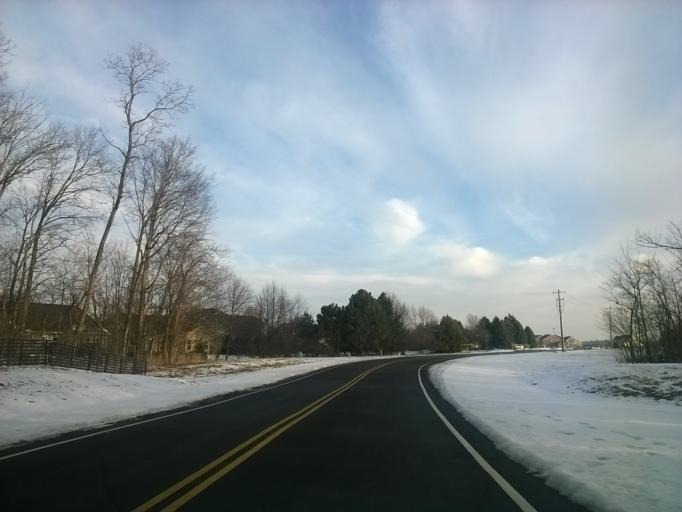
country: US
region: Indiana
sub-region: Hamilton County
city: Fishers
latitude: 39.9865
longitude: -86.0479
